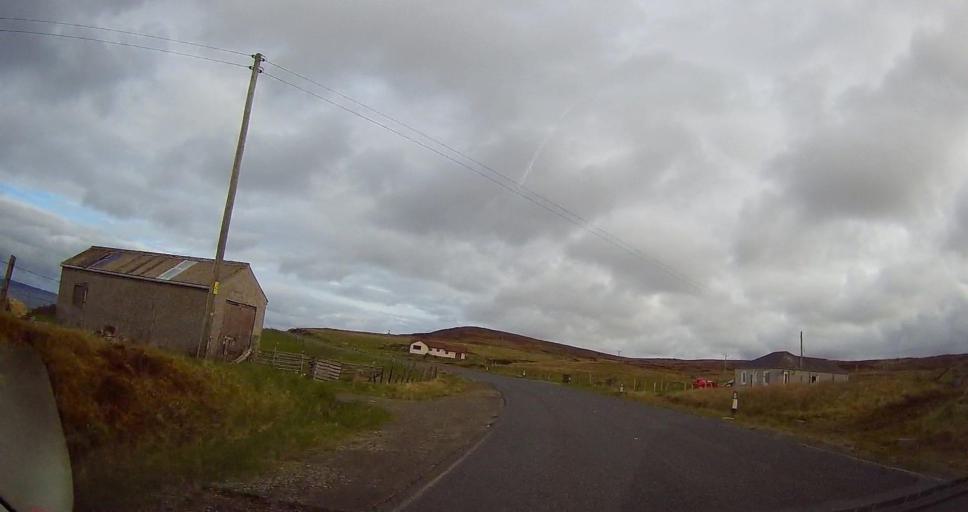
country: GB
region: Scotland
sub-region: Shetland Islands
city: Shetland
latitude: 60.5192
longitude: -1.1637
